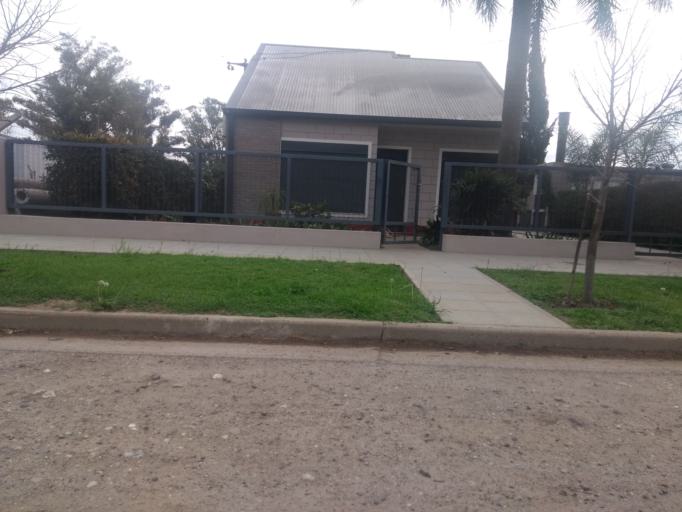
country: AR
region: Santa Fe
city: Galvez
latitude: -31.9083
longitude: -61.2797
